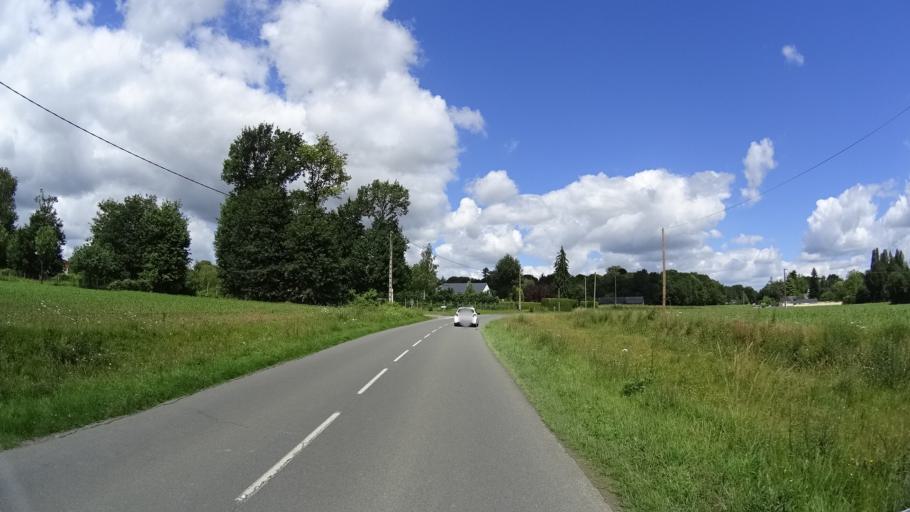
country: FR
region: Brittany
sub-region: Departement d'Ille-et-Vilaine
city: Saint-Gilles
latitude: 48.1447
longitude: -1.8294
